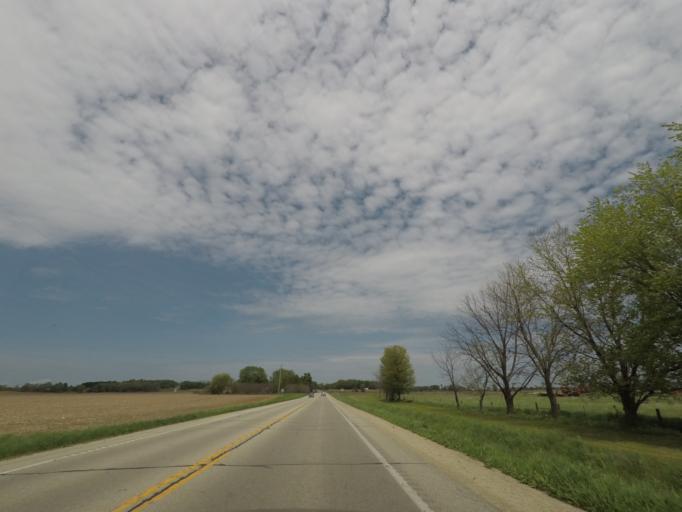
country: US
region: Wisconsin
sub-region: Rock County
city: Evansville
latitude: 42.8111
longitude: -89.2991
